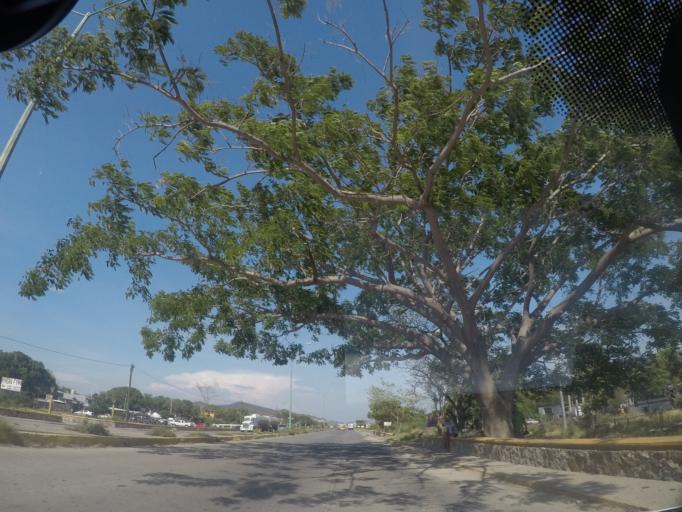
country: MX
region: Oaxaca
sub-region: Salina Cruz
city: Salina Cruz
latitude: 16.2208
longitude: -95.2005
